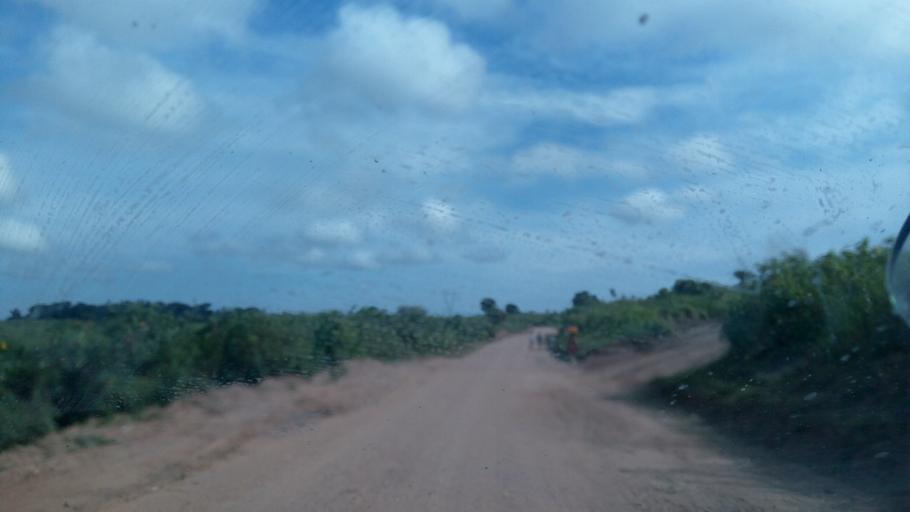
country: CD
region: Katanga
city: Kalemie
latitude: -5.8558
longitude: 29.1661
